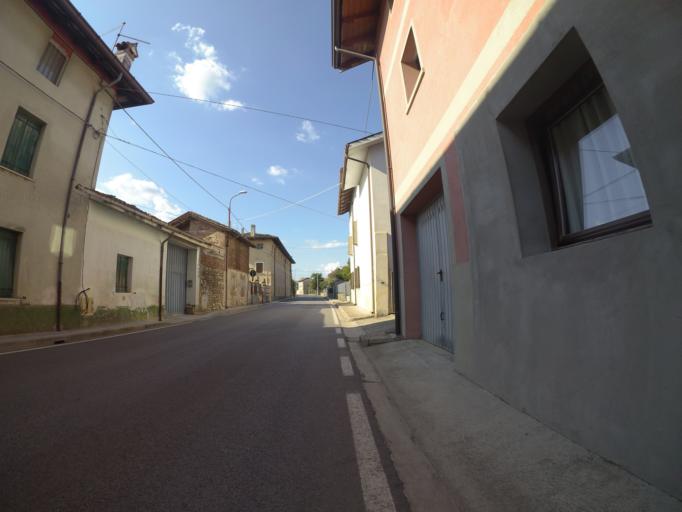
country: IT
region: Friuli Venezia Giulia
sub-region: Provincia di Udine
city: Pozzuolo del Friuli
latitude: 45.9964
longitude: 13.1754
